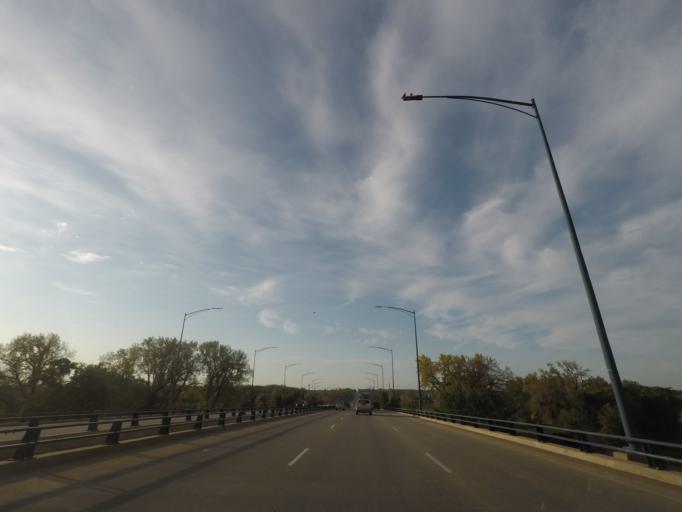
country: US
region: Iowa
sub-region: Polk County
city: Des Moines
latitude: 41.5828
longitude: -93.6449
